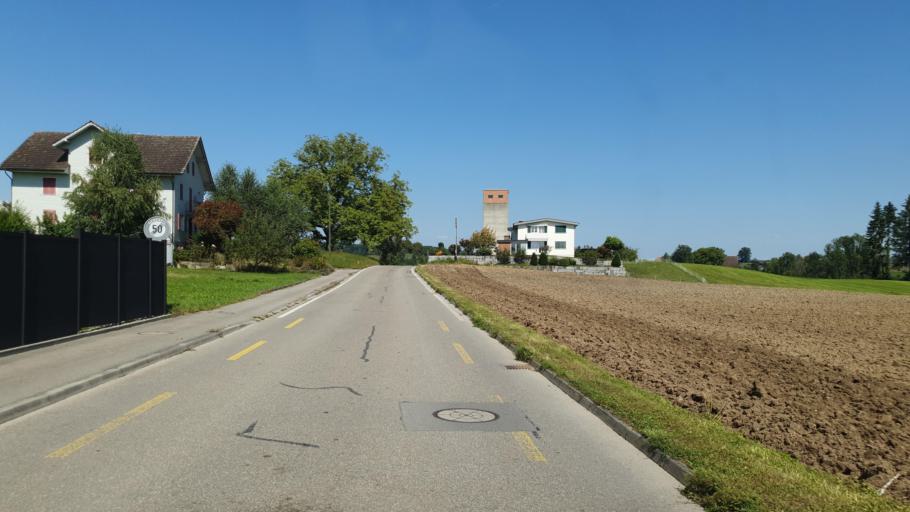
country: CH
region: Lucerne
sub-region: Hochdorf District
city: Ballwil
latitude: 47.1404
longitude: 8.3265
